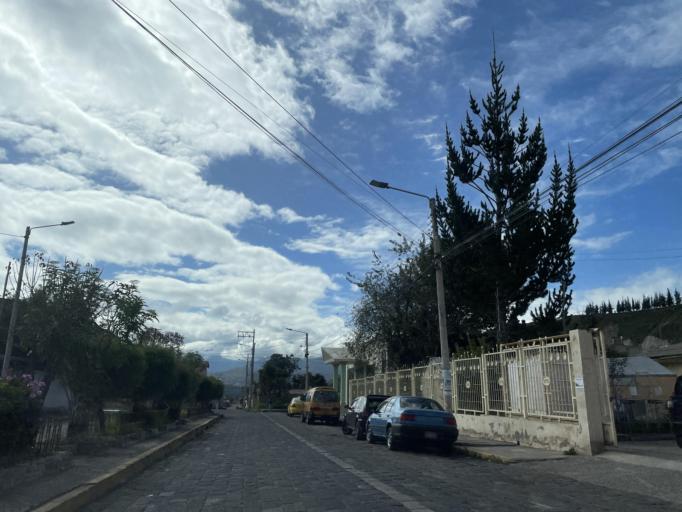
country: EC
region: Chimborazo
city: Guano
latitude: -1.6085
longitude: -78.6356
